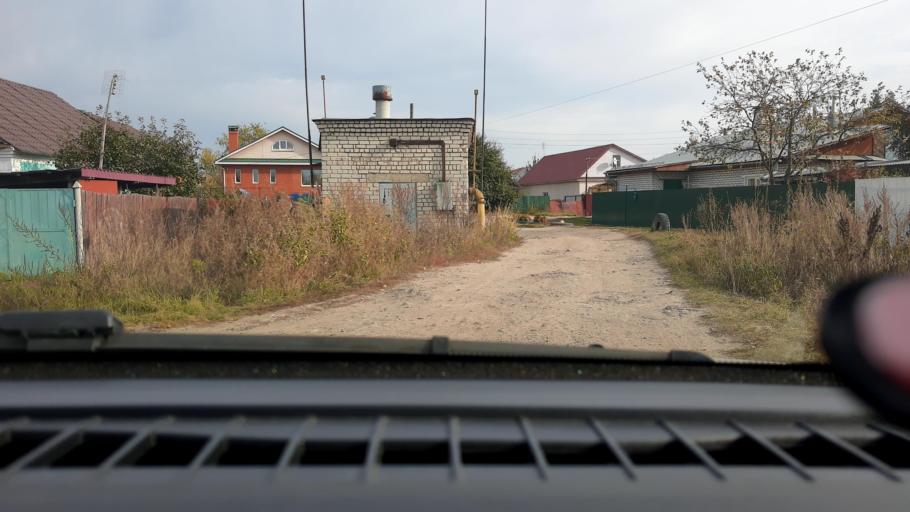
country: RU
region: Nizjnij Novgorod
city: Nizhniy Novgorod
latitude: 56.2853
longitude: 43.8960
